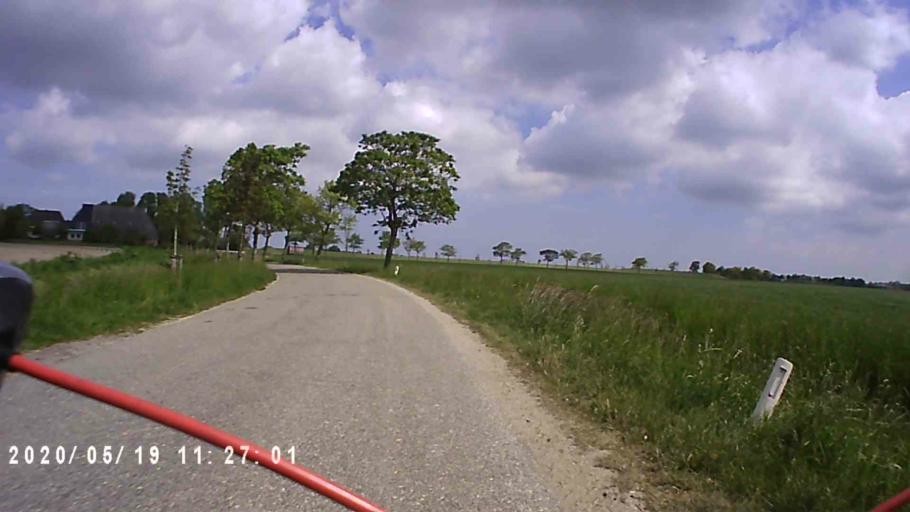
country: NL
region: Groningen
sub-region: Gemeente Zuidhorn
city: Oldehove
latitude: 53.3069
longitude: 6.3950
